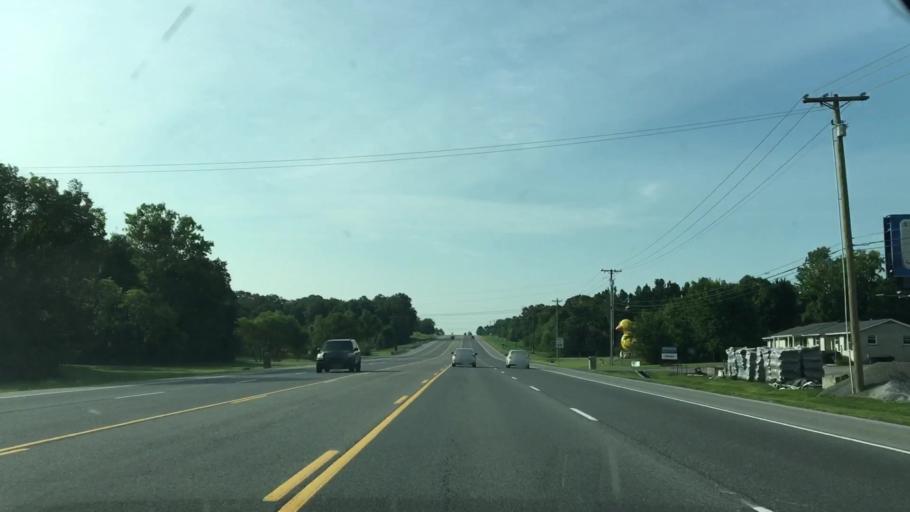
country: US
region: Tennessee
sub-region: Wilson County
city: Mount Juliet
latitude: 36.2178
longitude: -86.4234
